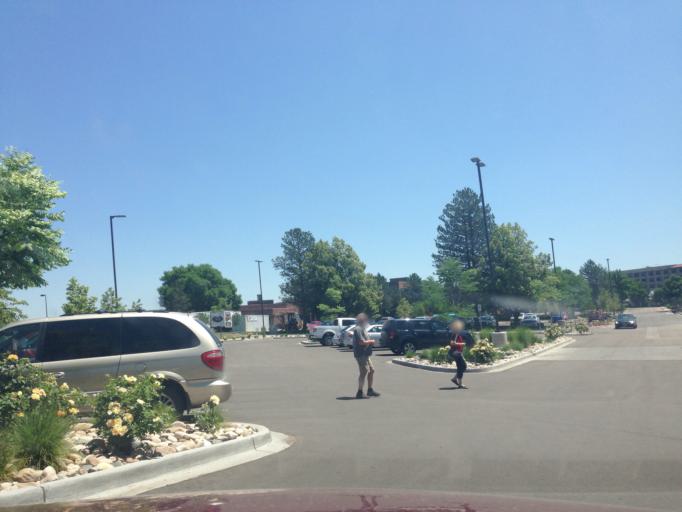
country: US
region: Colorado
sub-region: Larimer County
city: Fort Collins
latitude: 40.5398
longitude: -105.0761
